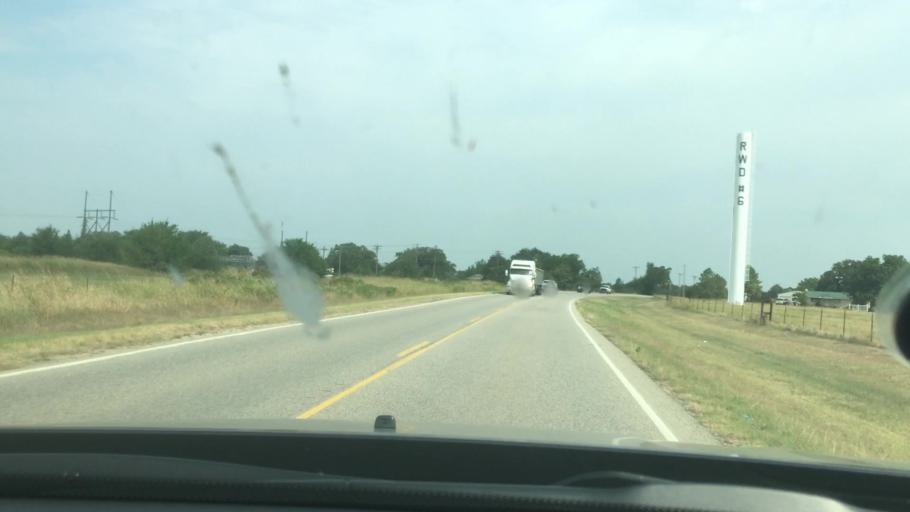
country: US
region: Oklahoma
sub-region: Bryan County
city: Durant
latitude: 34.1986
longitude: -96.4237
